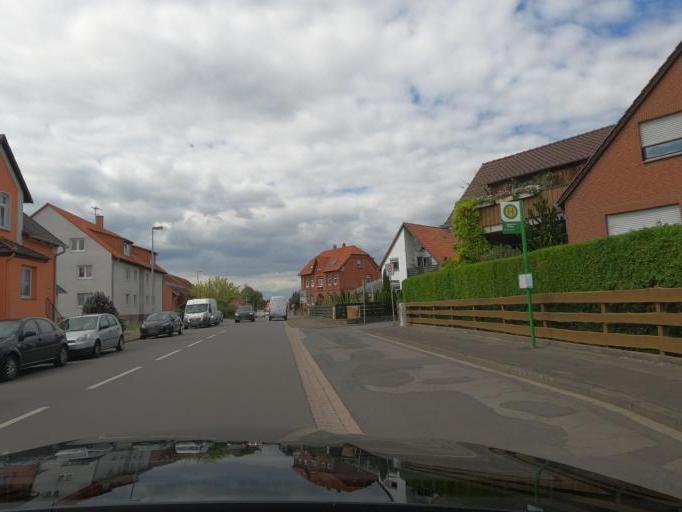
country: DE
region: Lower Saxony
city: Algermissen
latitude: 52.2530
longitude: 9.9807
